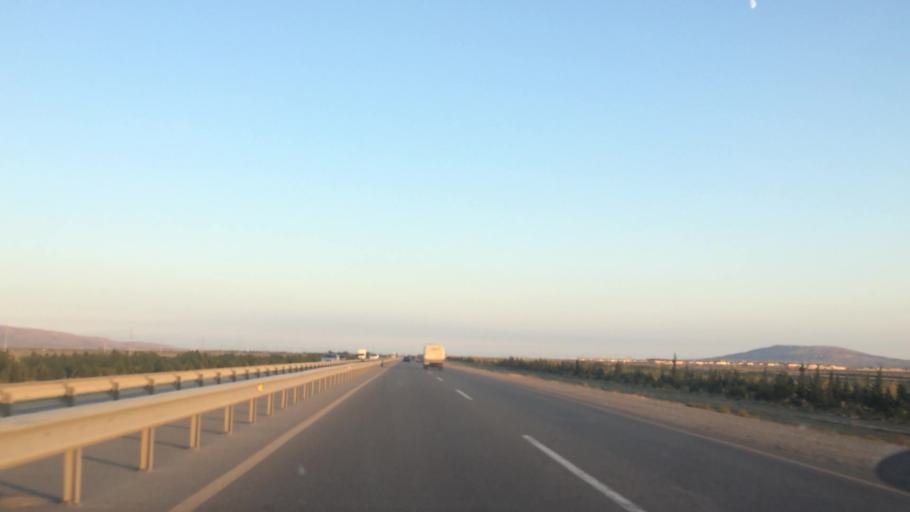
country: AZ
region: Baki
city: Qobustan
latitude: 39.9900
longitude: 49.1990
